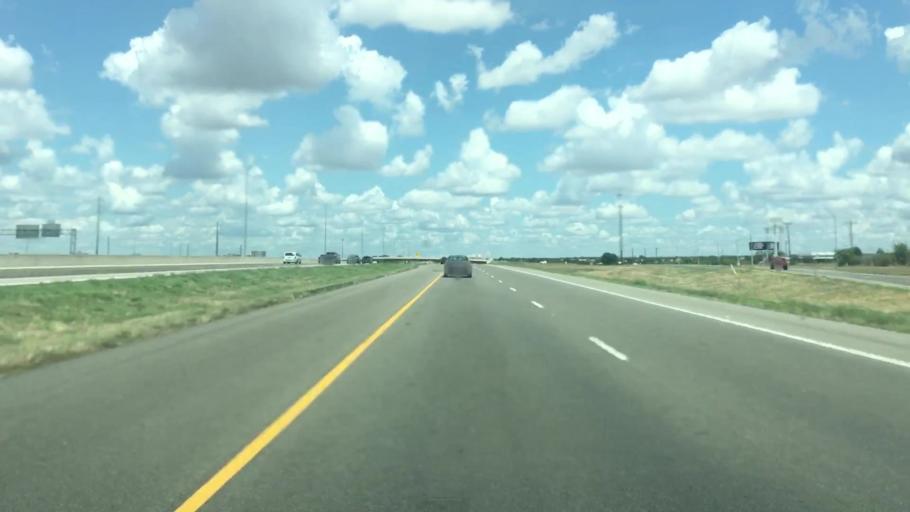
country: US
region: Texas
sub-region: Williamson County
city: Serenada
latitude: 30.6963
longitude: -97.6536
